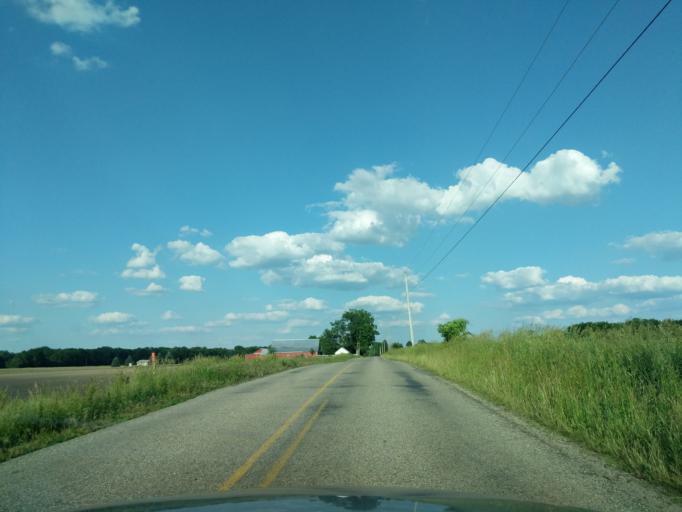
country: US
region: Indiana
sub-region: Whitley County
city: Tri-Lakes
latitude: 41.3023
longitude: -85.5244
